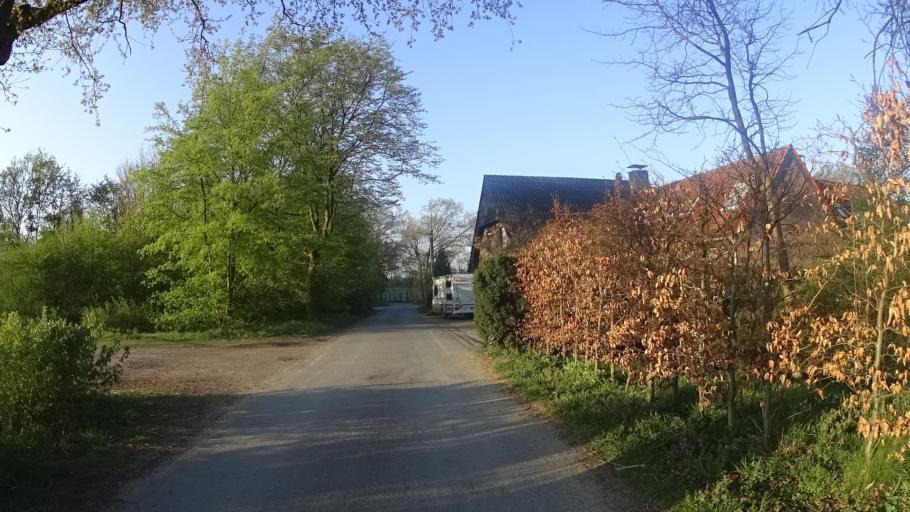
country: DE
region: North Rhine-Westphalia
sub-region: Regierungsbezirk Dusseldorf
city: Schermbeck
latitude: 51.6724
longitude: 6.8775
